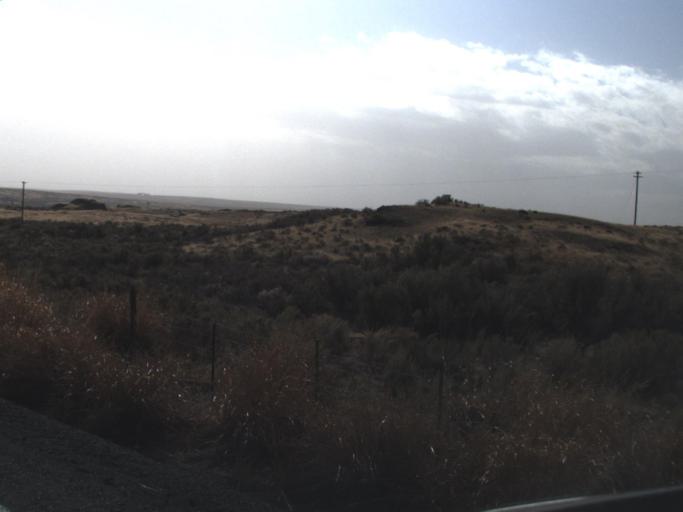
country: US
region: Washington
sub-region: Adams County
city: Ritzville
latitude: 47.3458
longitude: -118.6934
